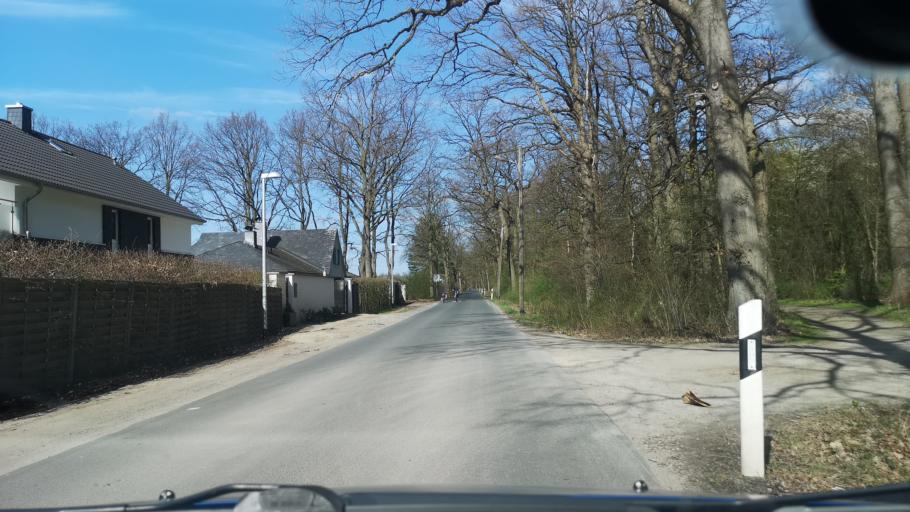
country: DE
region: Lower Saxony
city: Langenhagen
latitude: 52.4243
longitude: 9.7917
